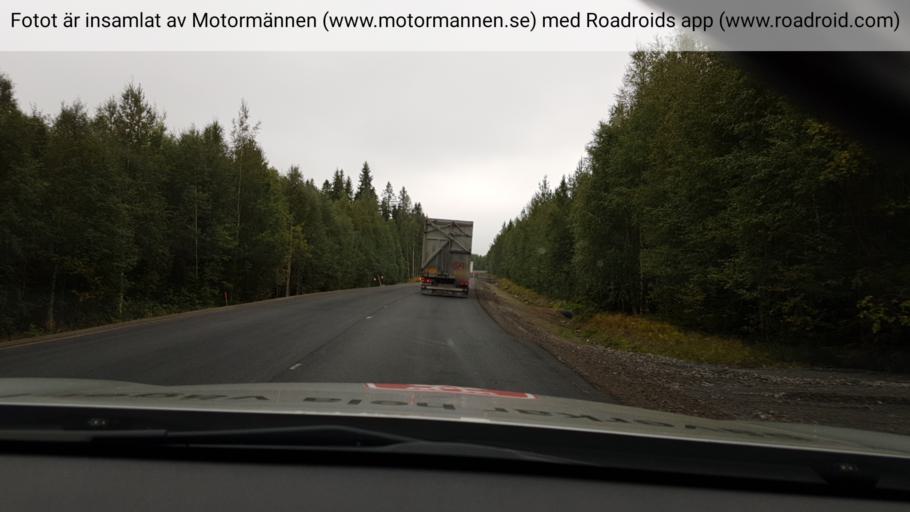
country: SE
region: Vaesterbotten
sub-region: Skelleftea Kommun
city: Burtraesk
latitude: 64.4005
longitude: 20.5487
